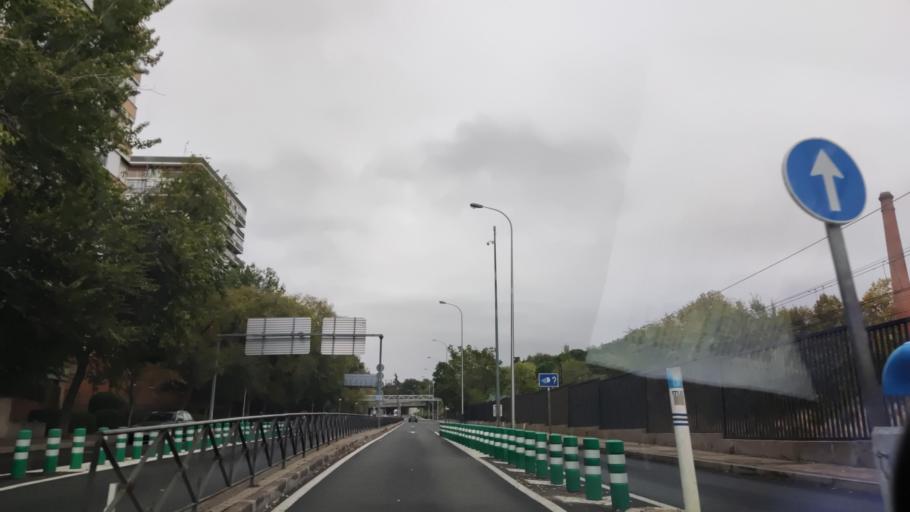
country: ES
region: Madrid
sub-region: Provincia de Madrid
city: Usera
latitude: 40.3882
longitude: -3.6884
